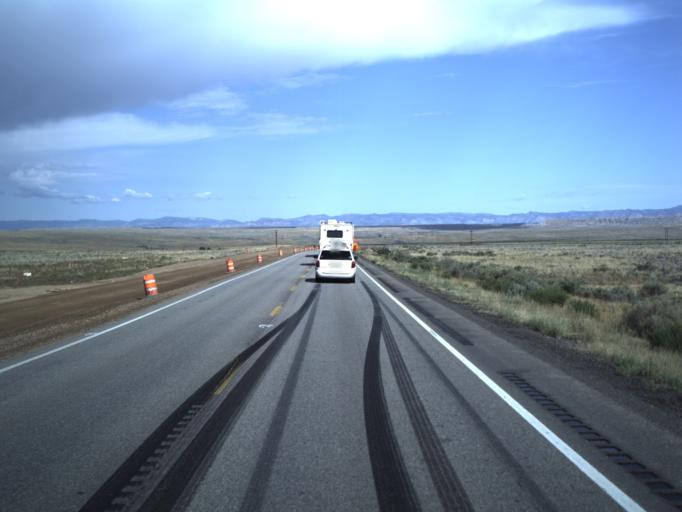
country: US
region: Utah
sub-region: Carbon County
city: East Carbon City
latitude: 39.4401
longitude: -110.4631
